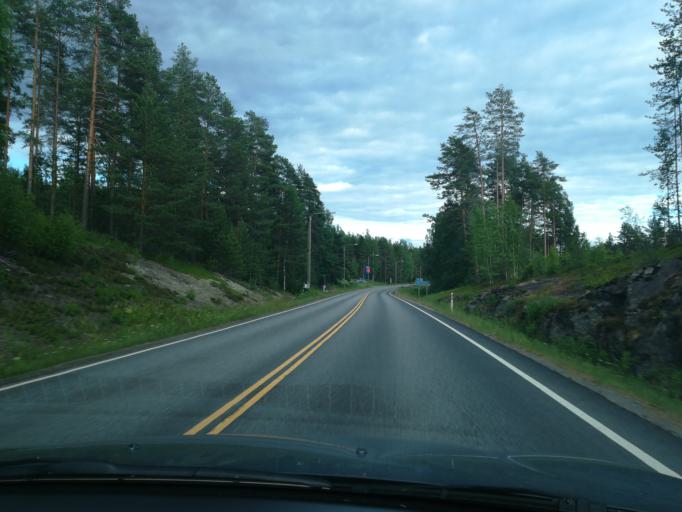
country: FI
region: Southern Savonia
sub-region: Pieksaemaeki
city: Juva
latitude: 61.5782
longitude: 27.6520
